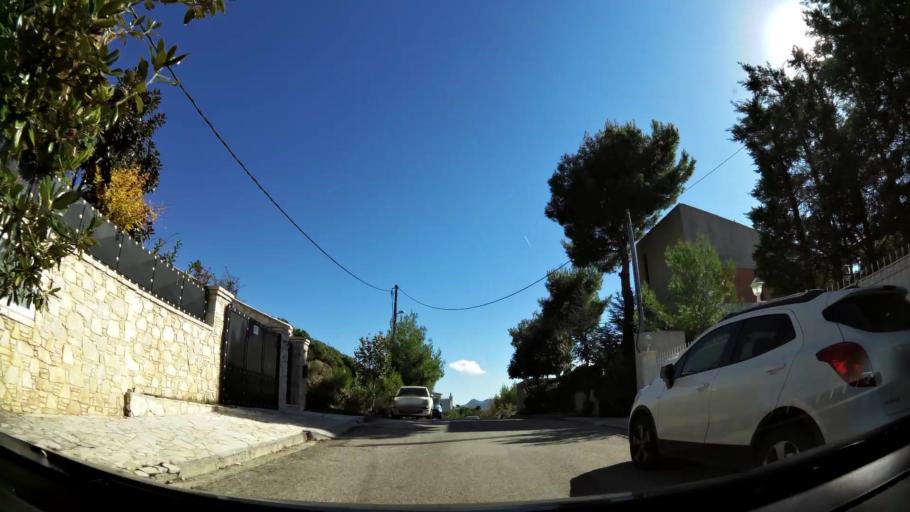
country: GR
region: Attica
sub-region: Nomarchia Anatolikis Attikis
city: Rodopoli
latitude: 38.1106
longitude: 23.8852
